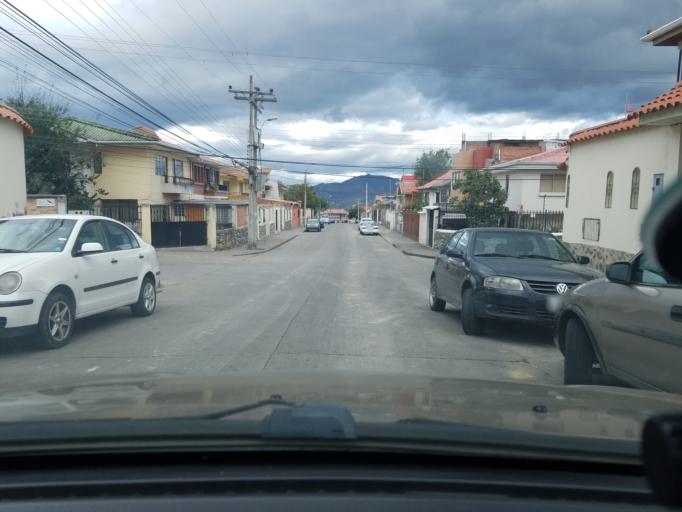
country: EC
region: Azuay
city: Cuenca
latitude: -2.8867
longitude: -78.9984
